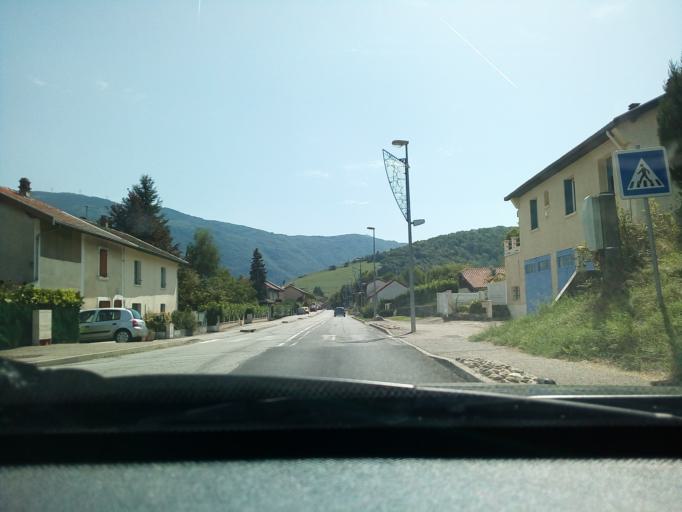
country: FR
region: Rhone-Alpes
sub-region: Departement de l'Isere
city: Brie-et-Angonnes
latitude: 45.1145
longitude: 5.7843
